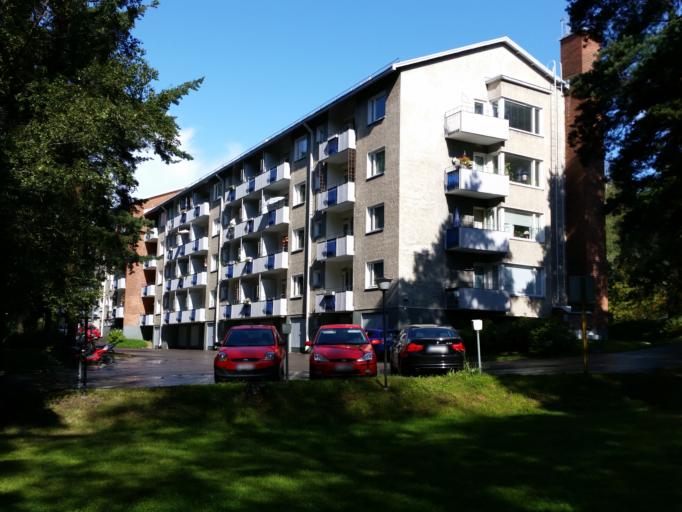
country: FI
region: Uusimaa
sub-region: Helsinki
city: Teekkarikylae
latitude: 60.2090
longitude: 24.8734
